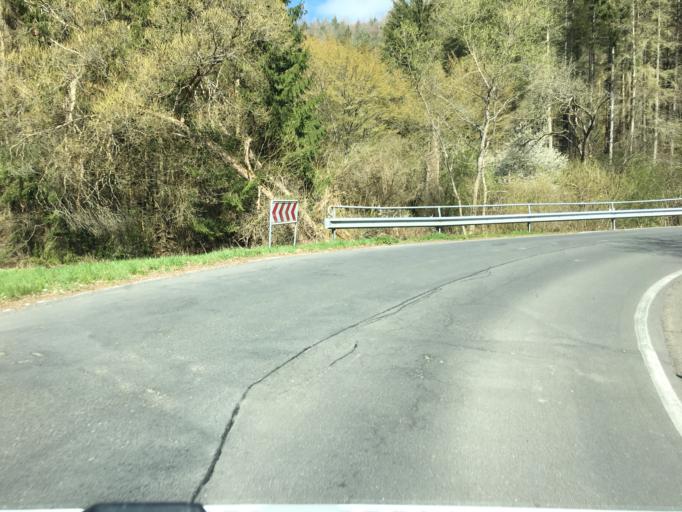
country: DE
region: Rheinland-Pfalz
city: Lind
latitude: 50.5144
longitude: 6.9574
